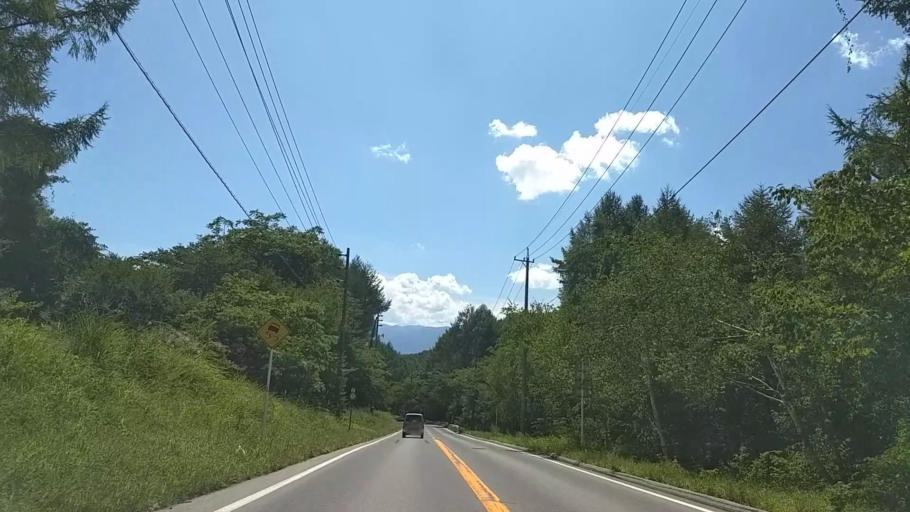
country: JP
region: Nagano
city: Chino
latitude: 36.0694
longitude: 138.2237
